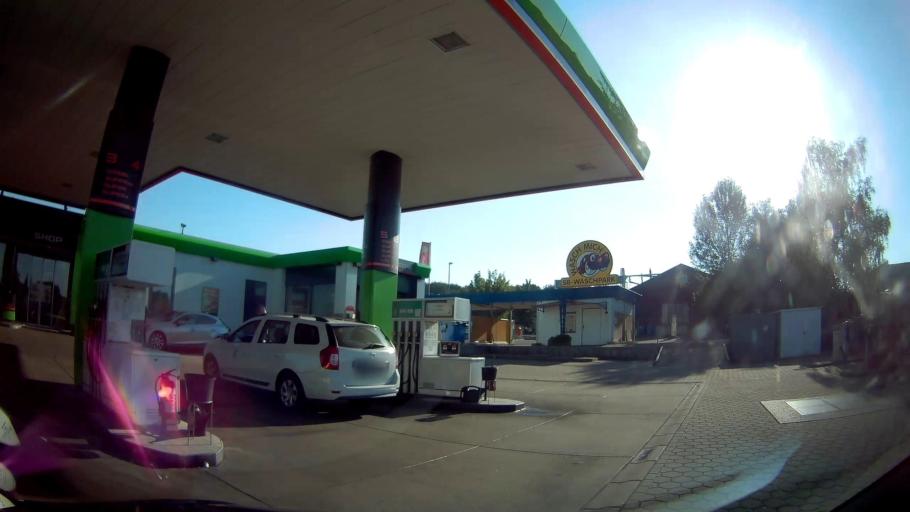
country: DE
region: North Rhine-Westphalia
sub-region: Regierungsbezirk Arnsberg
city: Dortmund
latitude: 51.5463
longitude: 7.4502
